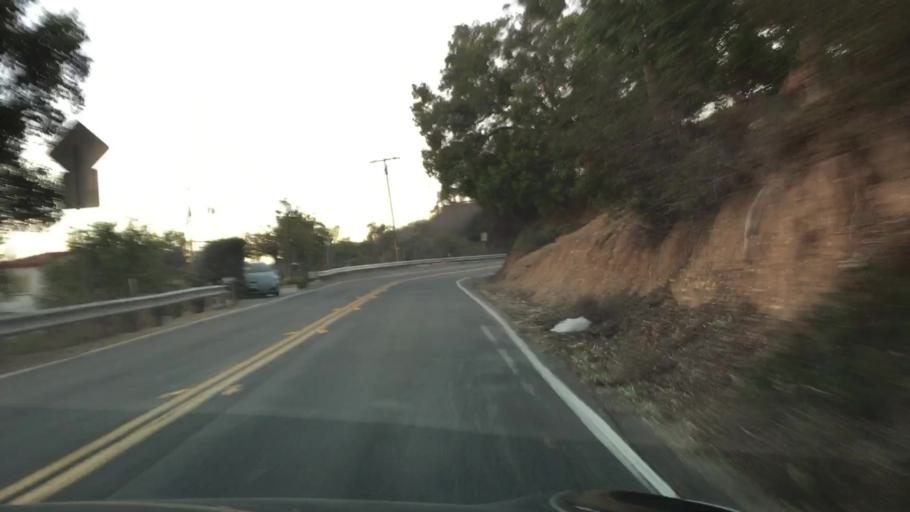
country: US
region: California
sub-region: Los Angeles County
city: Hacienda Heights
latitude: 33.9934
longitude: -117.9915
